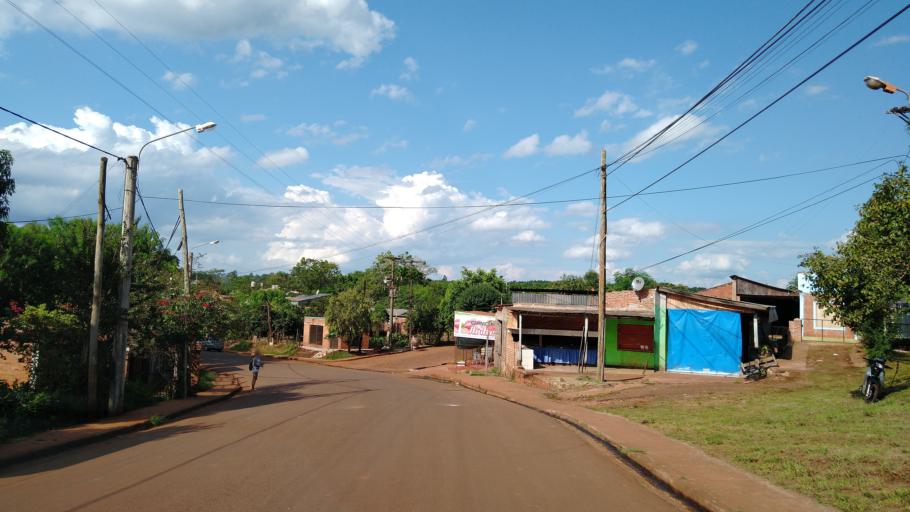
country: AR
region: Misiones
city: Puerto Piray
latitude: -26.4684
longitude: -54.7065
